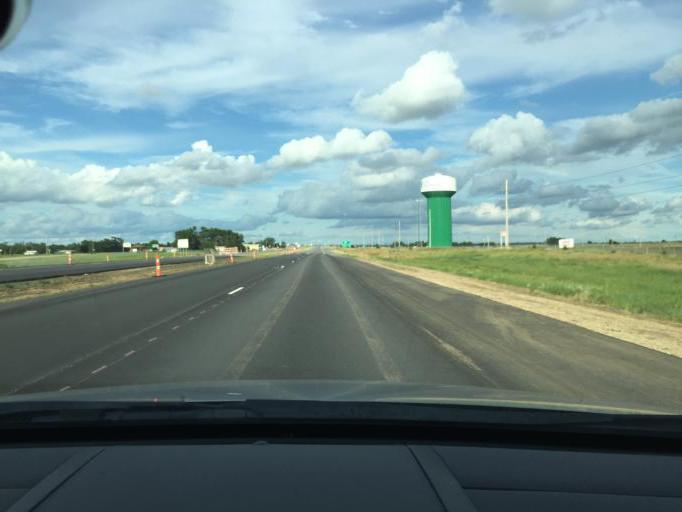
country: US
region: Kansas
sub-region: Reno County
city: South Hutchinson
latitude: 38.0130
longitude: -97.9488
